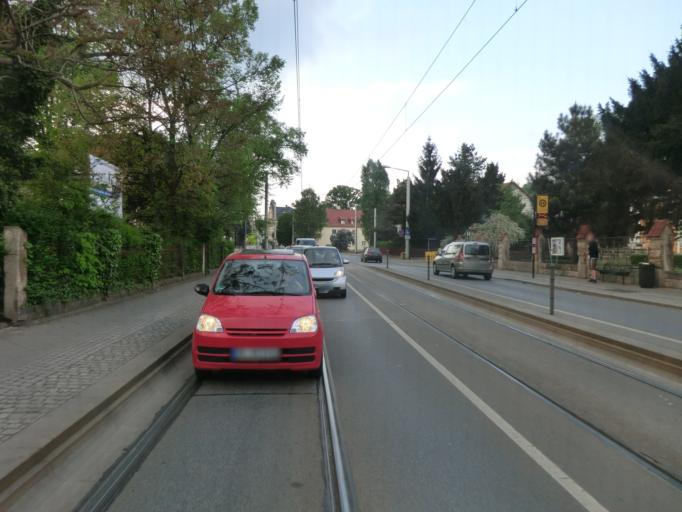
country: DE
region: Saxony
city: Albertstadt
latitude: 51.0492
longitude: 13.8098
